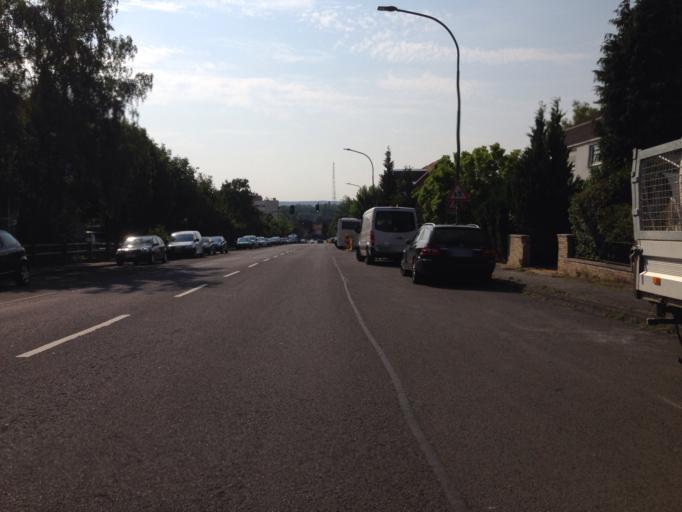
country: DE
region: Hesse
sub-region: Regierungsbezirk Giessen
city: Giessen
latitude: 50.6026
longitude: 8.6941
